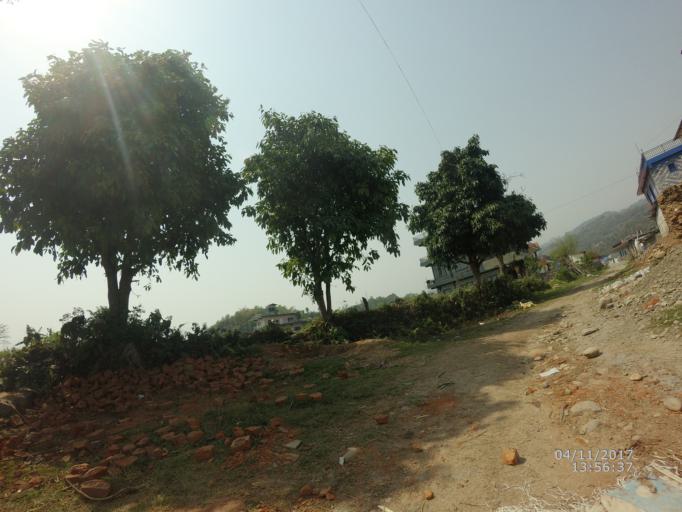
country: NP
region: Western Region
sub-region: Gandaki Zone
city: Pokhara
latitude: 28.1859
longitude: 84.0425
